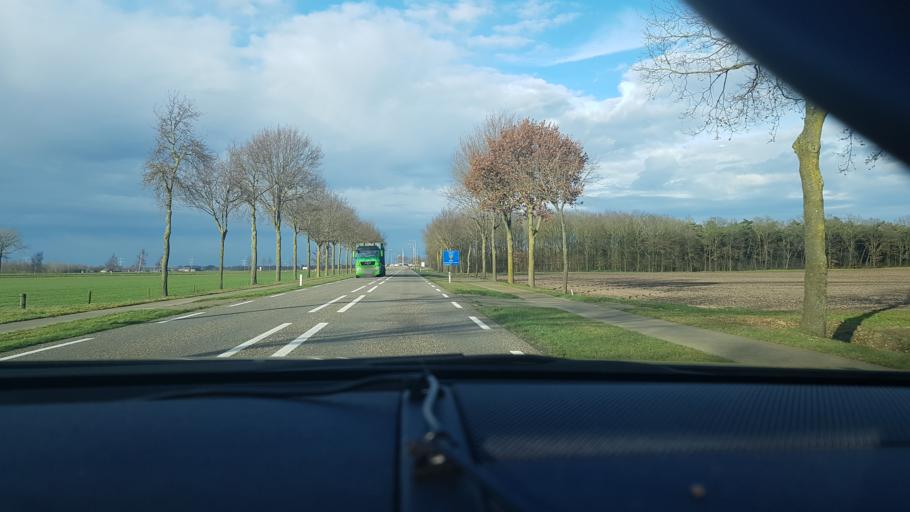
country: NL
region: Limburg
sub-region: Gemeente Peel en Maas
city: Maasbree
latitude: 51.4057
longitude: 5.9657
